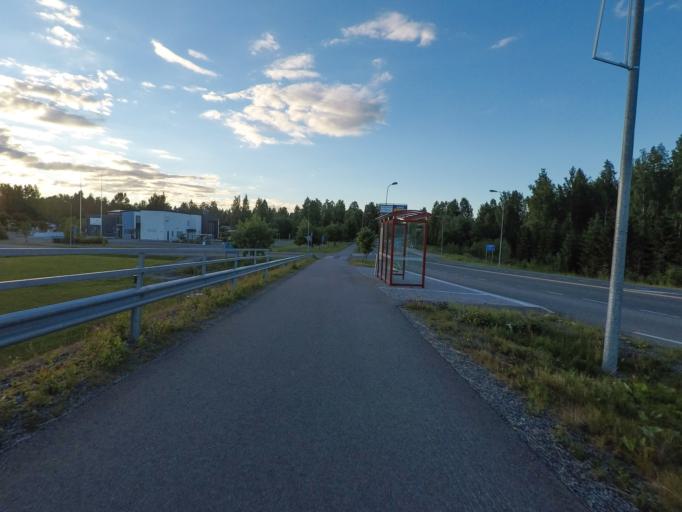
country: FI
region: Northern Savo
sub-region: Kuopio
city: Kuopio
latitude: 62.9740
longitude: 27.7025
